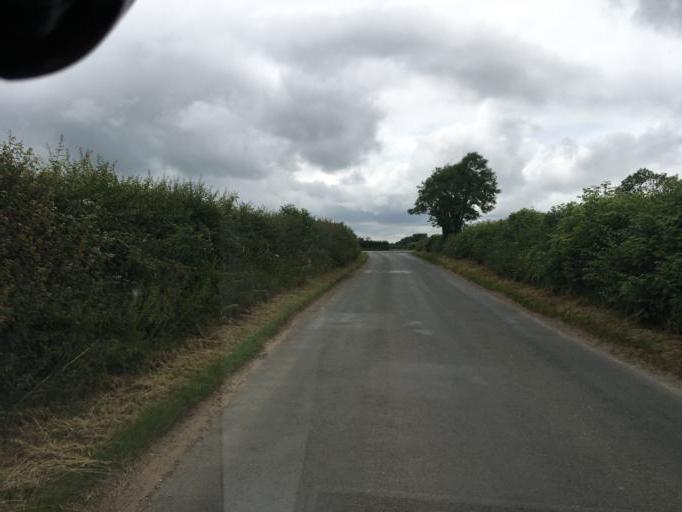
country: GB
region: England
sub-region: Gloucestershire
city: Stonehouse
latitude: 51.7023
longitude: -2.2936
